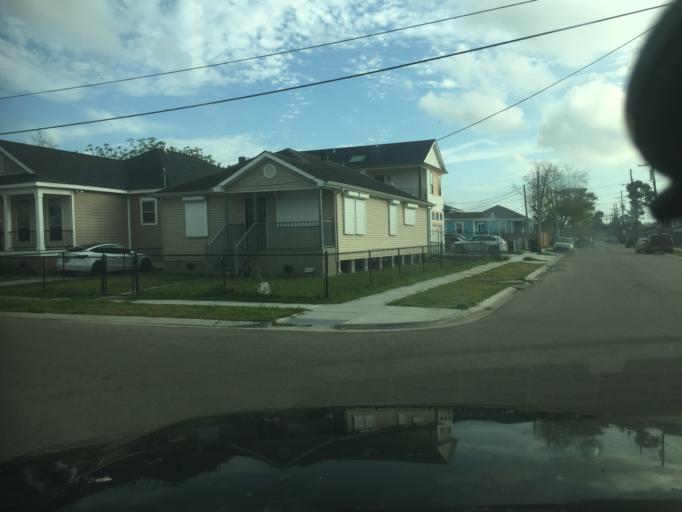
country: US
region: Louisiana
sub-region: Orleans Parish
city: New Orleans
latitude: 29.9966
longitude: -90.0819
